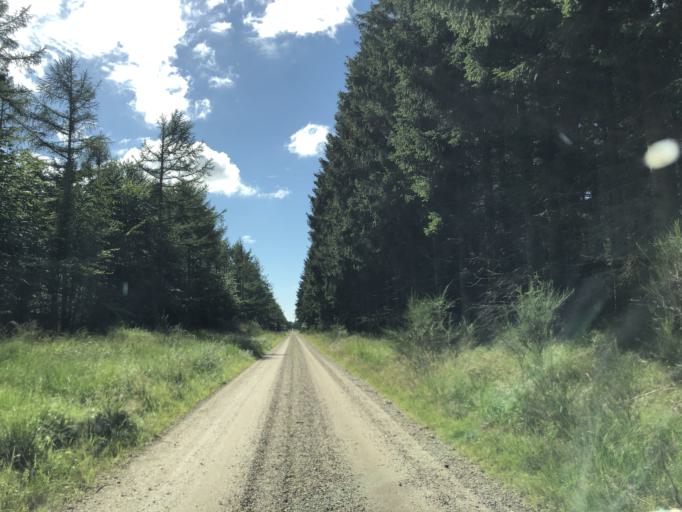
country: DK
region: Central Jutland
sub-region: Holstebro Kommune
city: Ulfborg
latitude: 56.2316
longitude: 8.4862
